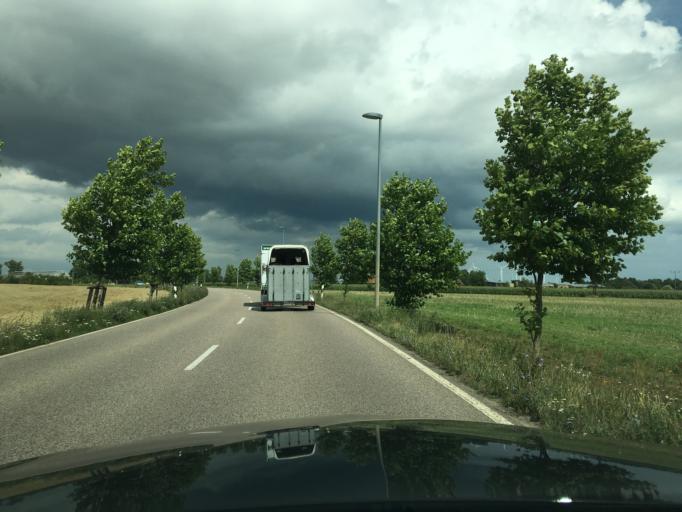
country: DE
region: Saxony-Anhalt
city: Brehna
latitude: 51.5584
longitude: 12.1980
